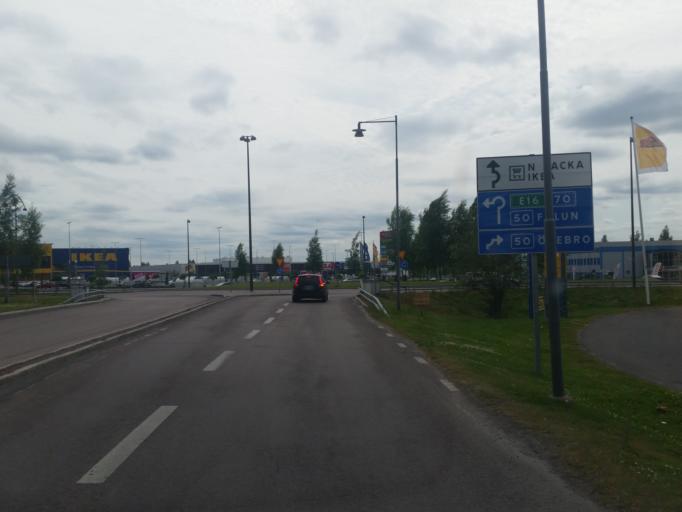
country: SE
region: Dalarna
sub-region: Borlange Kommun
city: Borlaenge
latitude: 60.4823
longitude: 15.4152
